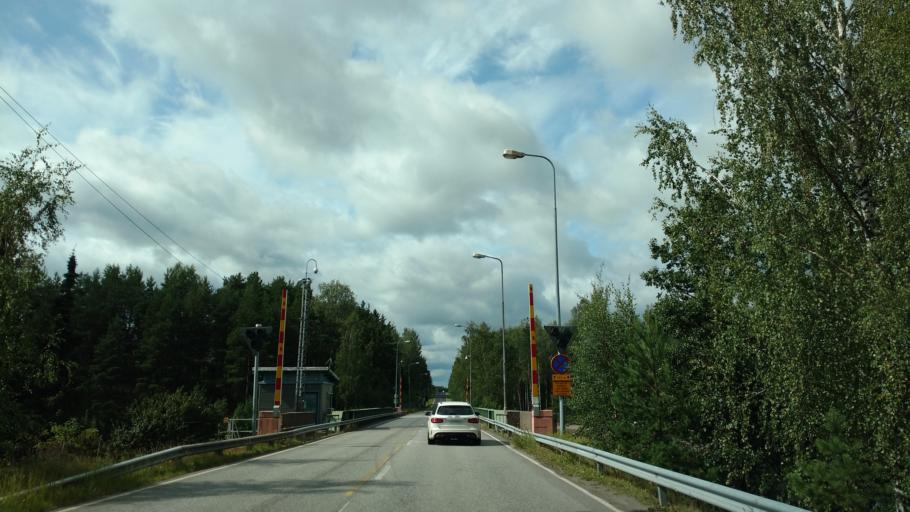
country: FI
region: Varsinais-Suomi
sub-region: Salo
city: Saerkisalo
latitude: 60.1880
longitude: 22.8693
